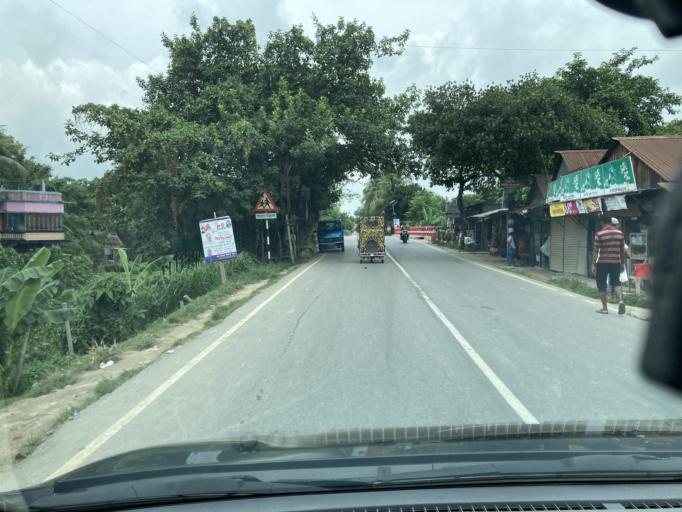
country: BD
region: Dhaka
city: Azimpur
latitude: 23.8060
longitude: 90.2079
